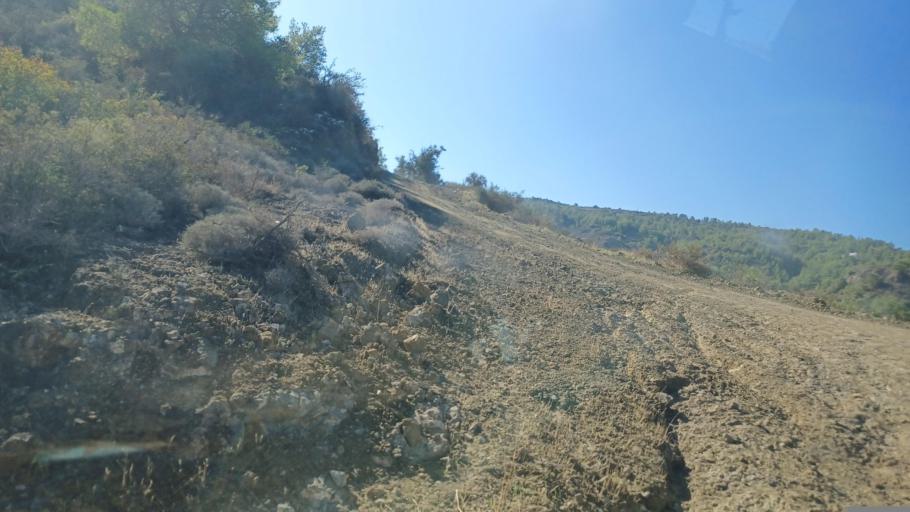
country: CY
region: Pafos
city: Polis
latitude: 35.0231
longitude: 32.4912
